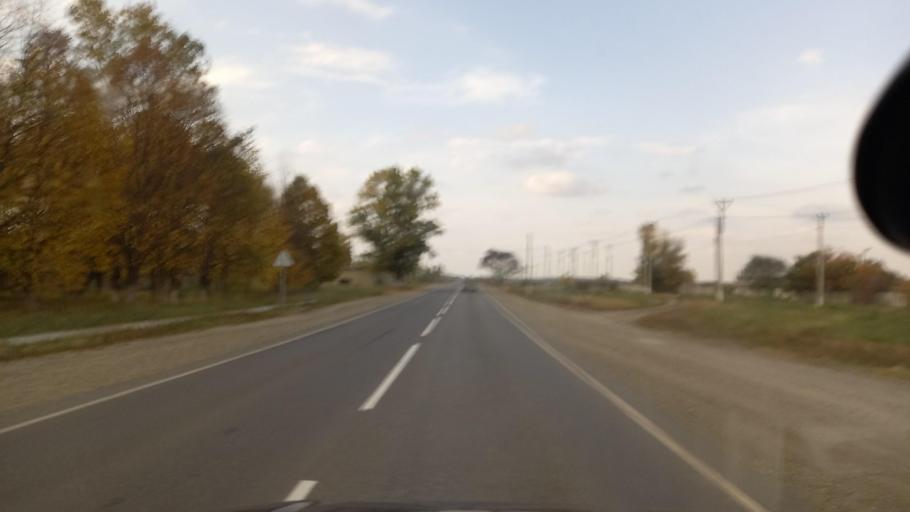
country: RU
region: Krasnodarskiy
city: Mostovskoy
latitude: 44.3760
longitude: 40.8243
